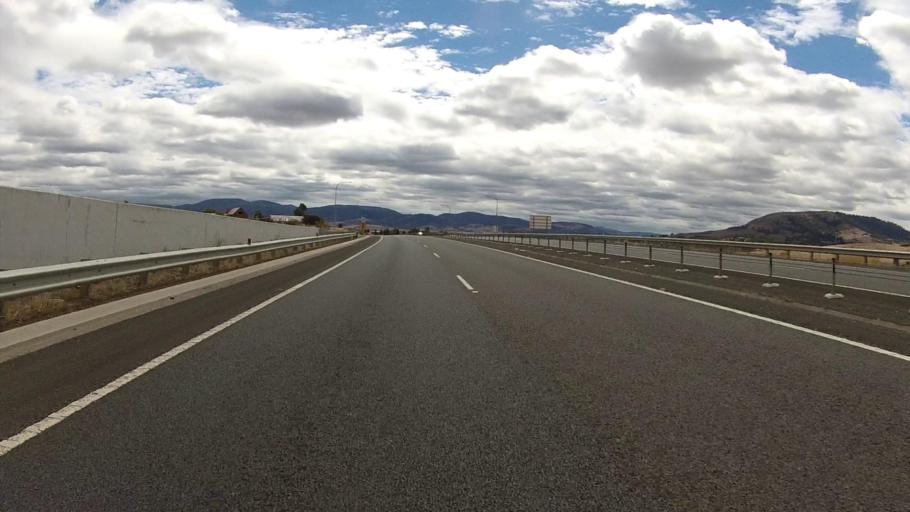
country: AU
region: Tasmania
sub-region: Brighton
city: Bridgewater
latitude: -42.7135
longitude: 147.2457
